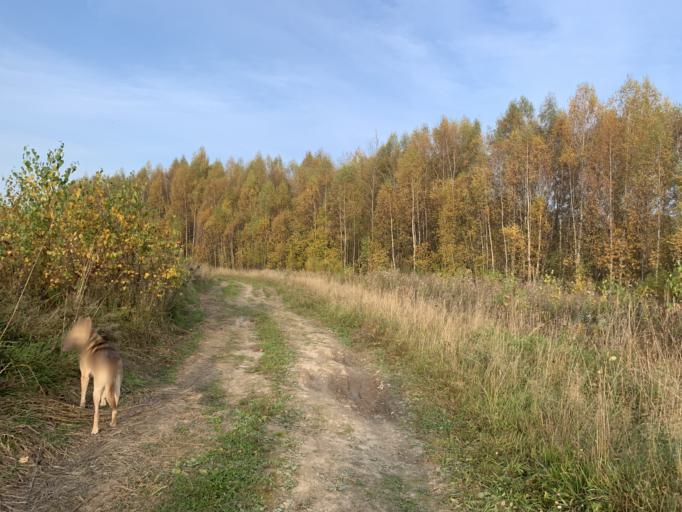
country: RU
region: Jaroslavl
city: Porech'ye-Rybnoye
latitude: 56.9841
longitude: 39.3844
